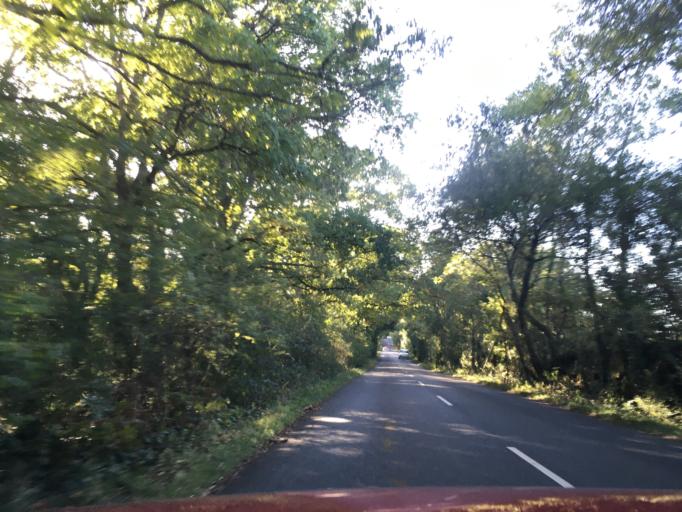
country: GB
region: England
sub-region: Hampshire
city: Swanmore
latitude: 50.9316
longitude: -1.1747
